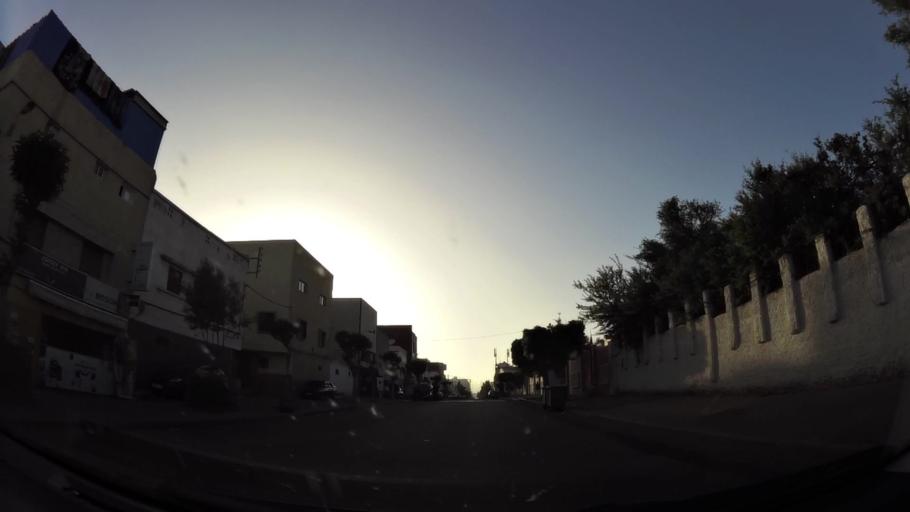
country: MA
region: Oued ed Dahab-Lagouira
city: Dakhla
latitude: 30.4168
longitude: -9.5695
